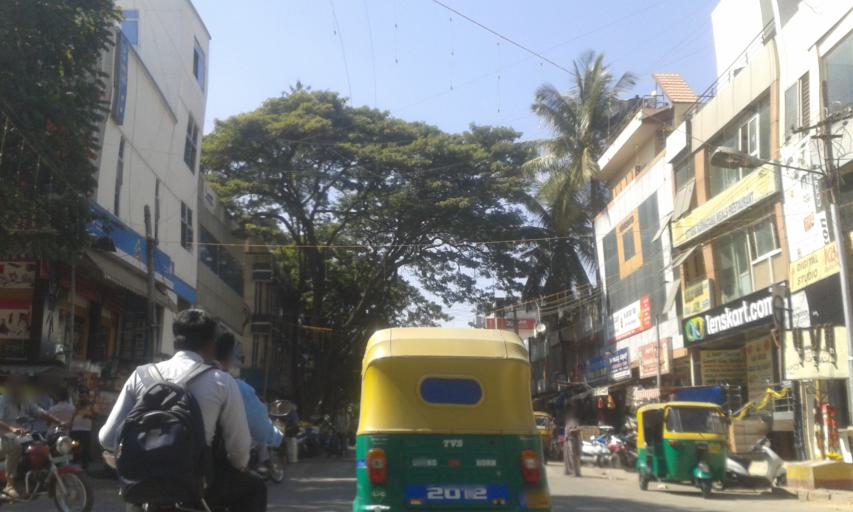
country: IN
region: Karnataka
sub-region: Bangalore Urban
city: Bangalore
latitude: 12.9190
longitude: 77.5927
